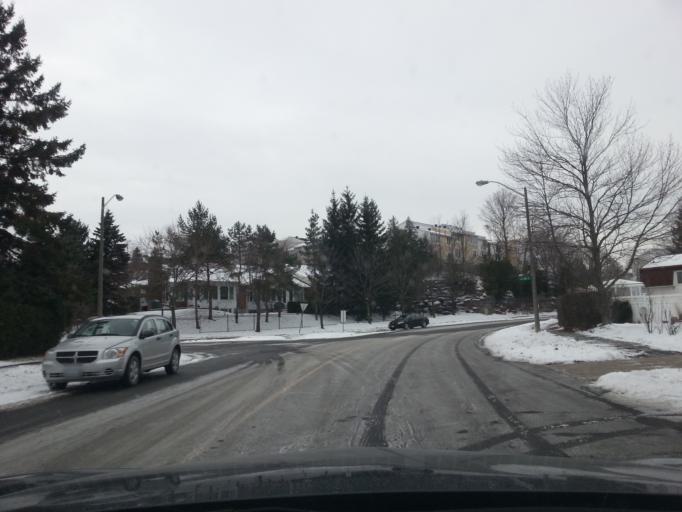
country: CA
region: Ontario
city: Ottawa
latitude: 45.3552
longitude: -75.6706
